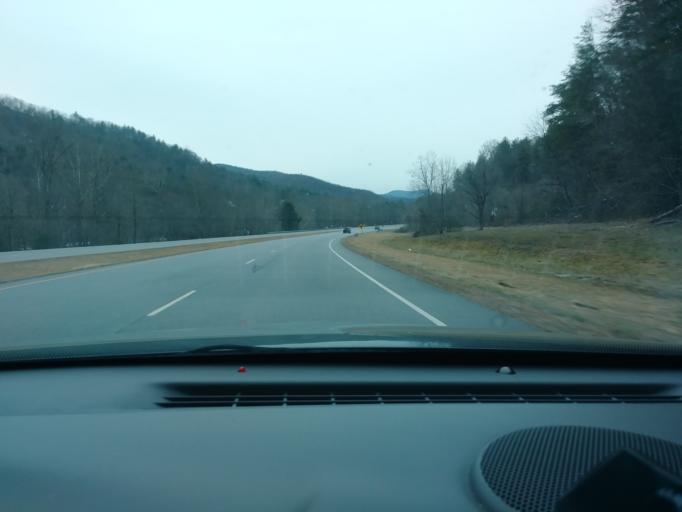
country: US
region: North Carolina
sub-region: Wilkes County
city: Millers Creek
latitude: 36.1811
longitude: -81.3953
